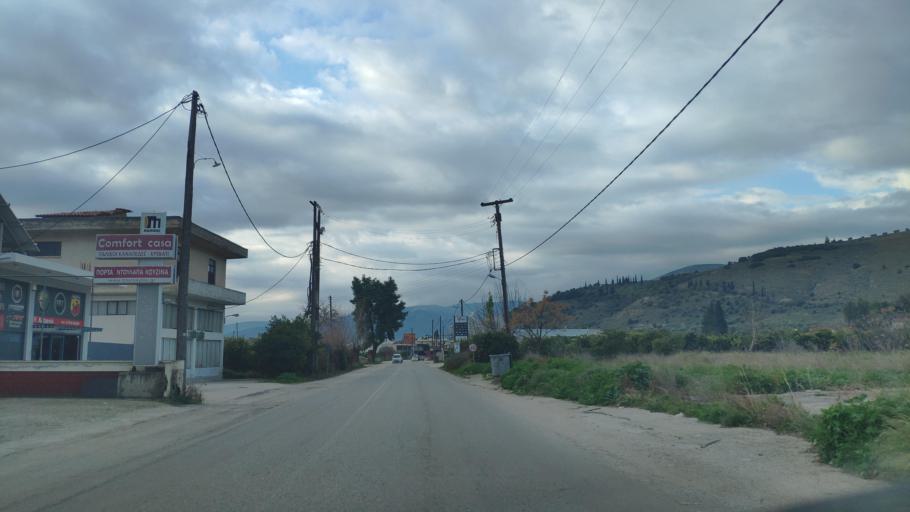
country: GR
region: Peloponnese
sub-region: Nomos Argolidos
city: Argos
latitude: 37.6252
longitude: 22.7172
